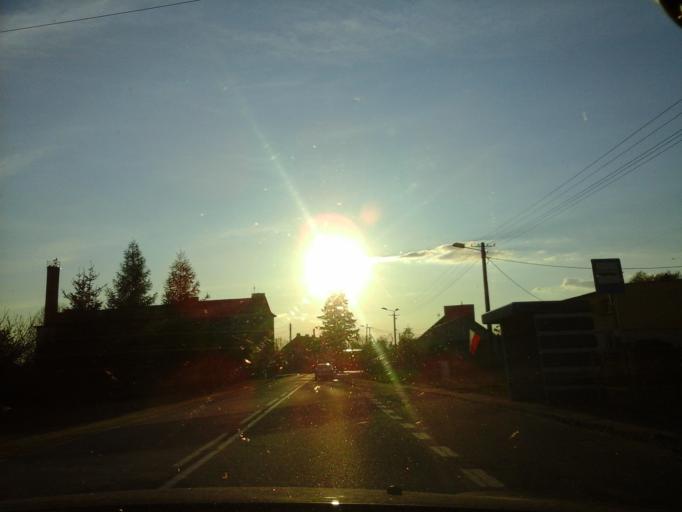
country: PL
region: West Pomeranian Voivodeship
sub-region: Powiat choszczenski
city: Krzecin
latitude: 53.1181
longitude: 15.5737
